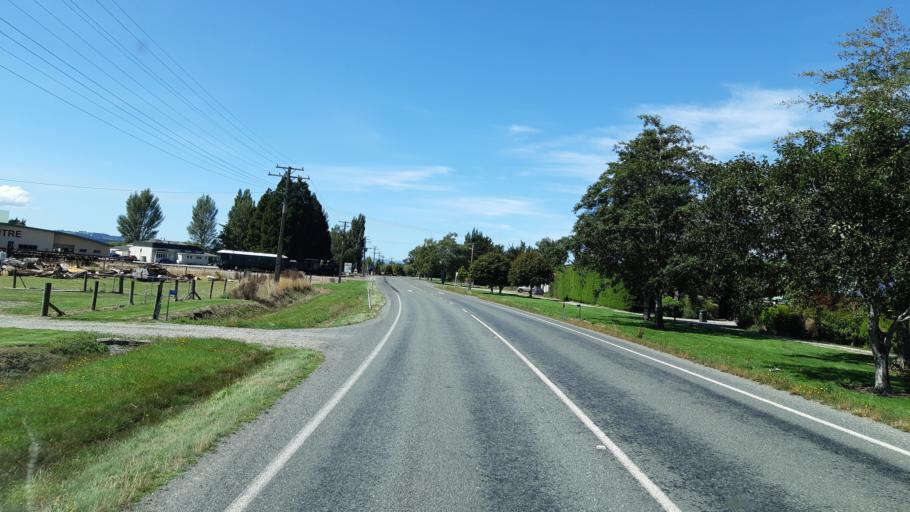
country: NZ
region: Southland
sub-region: Gore District
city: Gore
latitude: -45.9927
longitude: 168.8082
